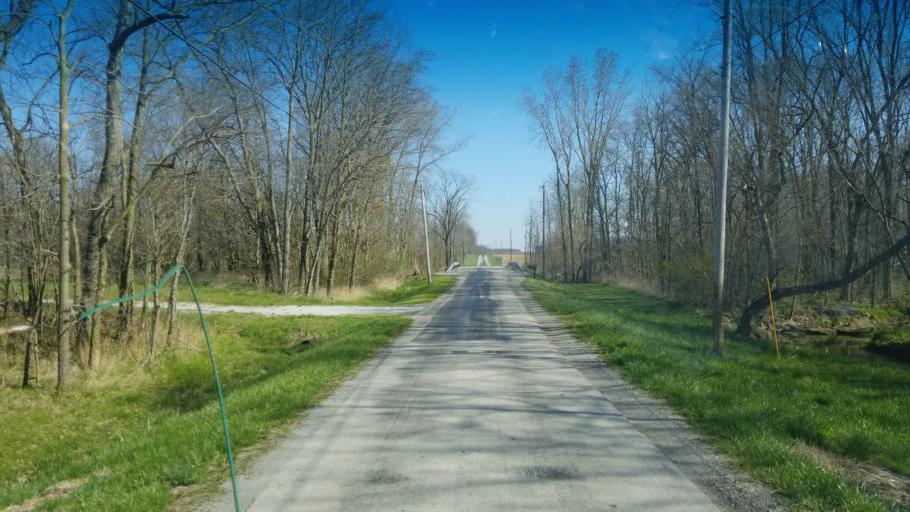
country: US
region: Ohio
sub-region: Hardin County
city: Forest
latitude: 40.7108
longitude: -83.4452
